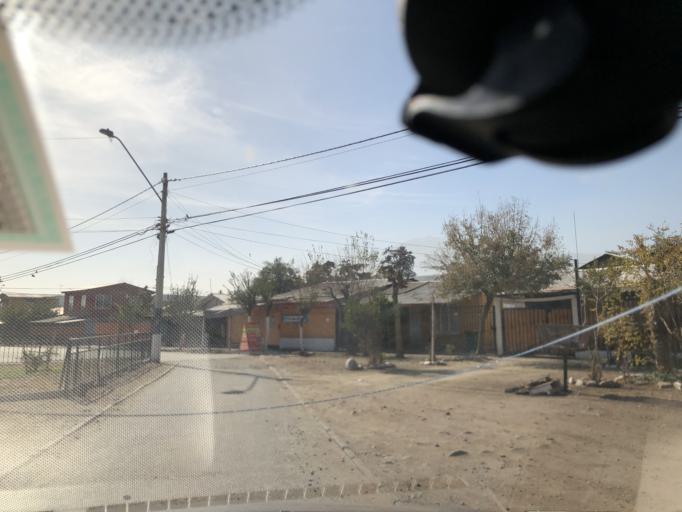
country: CL
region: Santiago Metropolitan
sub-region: Provincia de Cordillera
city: Puente Alto
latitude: -33.6171
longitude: -70.5616
